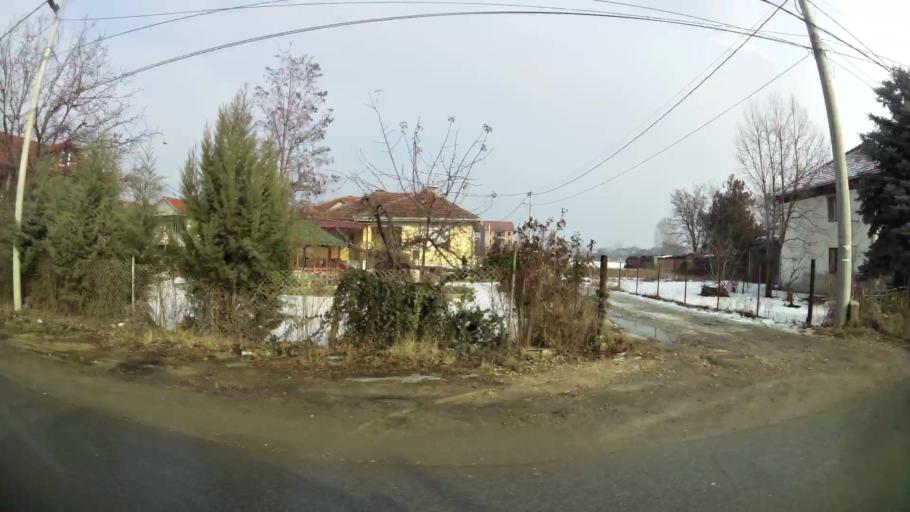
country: MK
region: Ilinden
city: Marino
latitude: 41.9934
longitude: 21.5888
